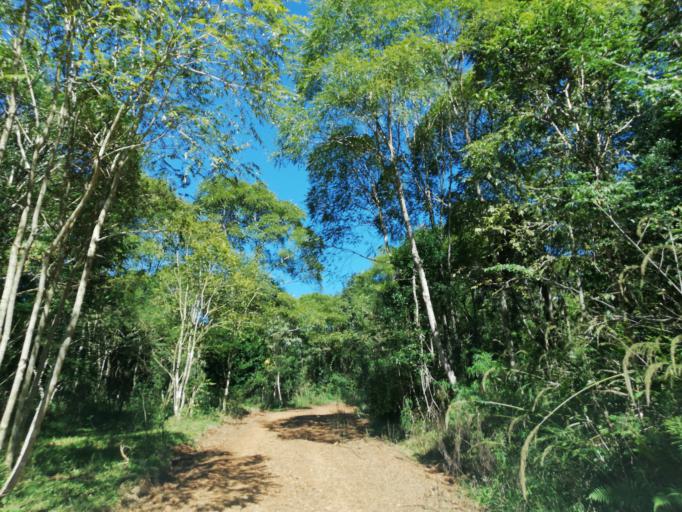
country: AR
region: Misiones
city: El Soberbio
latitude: -27.0631
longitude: -54.3744
